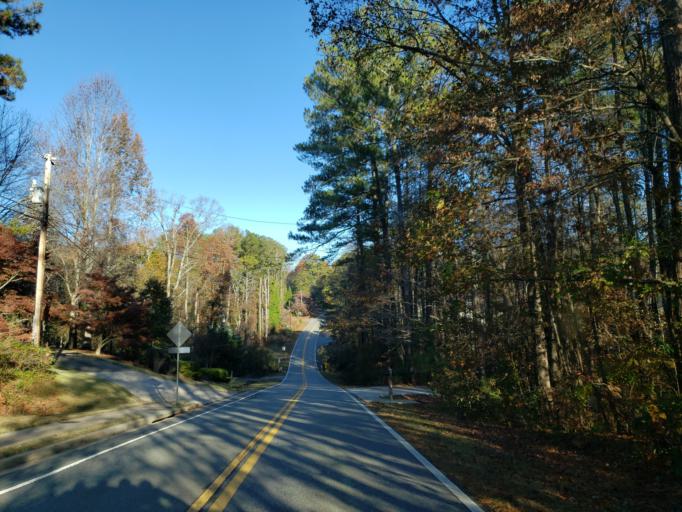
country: US
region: Georgia
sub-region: Cherokee County
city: Woodstock
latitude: 34.0461
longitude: -84.4694
